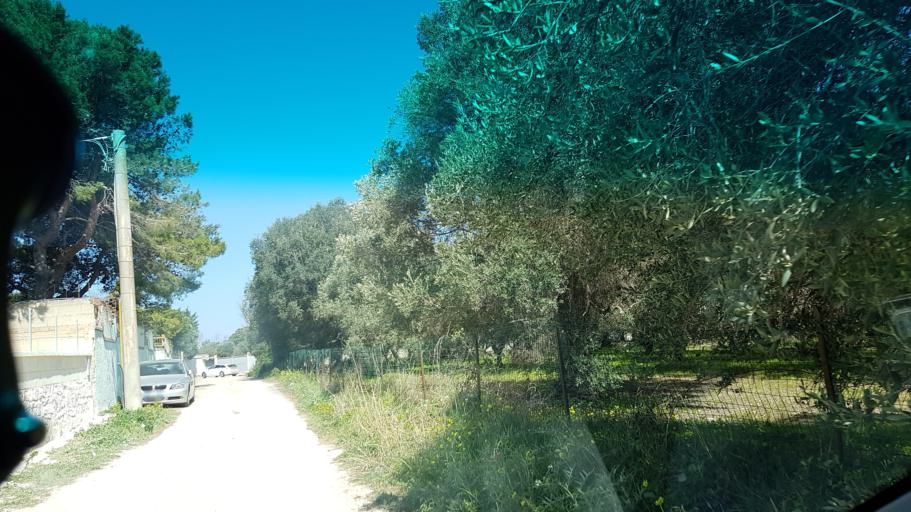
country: IT
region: Apulia
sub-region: Provincia di Brindisi
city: Brindisi
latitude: 40.6534
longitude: 17.9286
